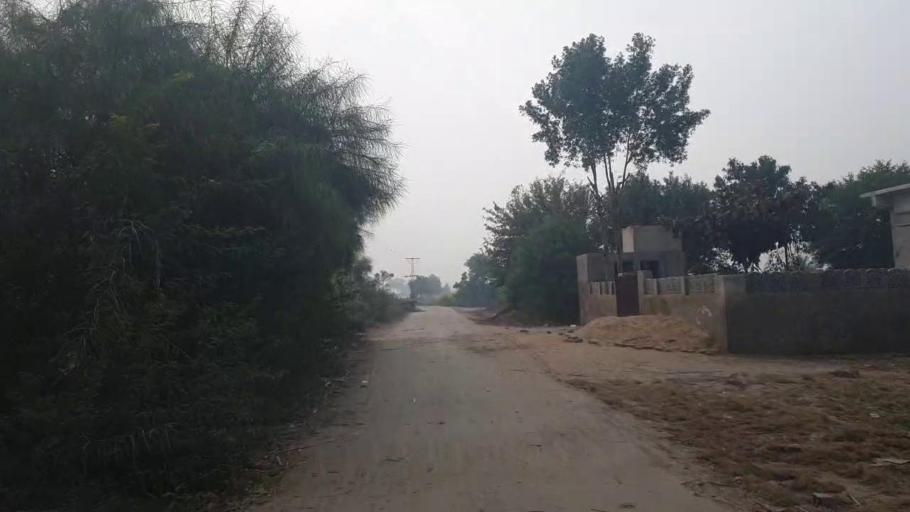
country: PK
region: Sindh
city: Tando Adam
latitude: 25.7195
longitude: 68.6803
